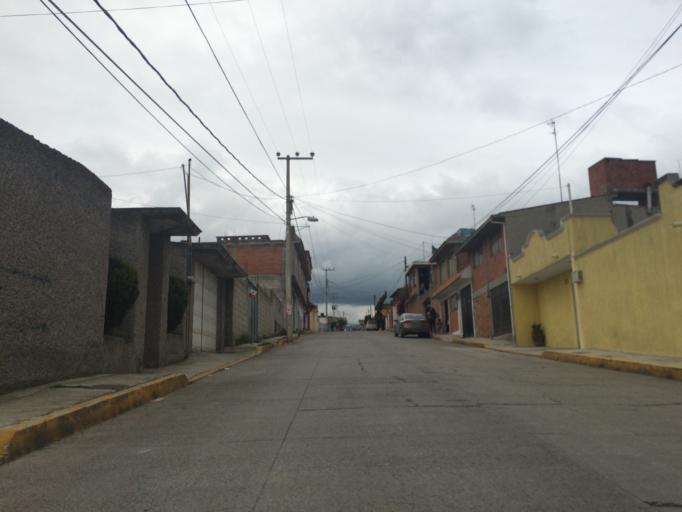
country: MX
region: Mexico
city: San Juan de las Huertas
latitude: 19.2480
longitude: -99.7459
